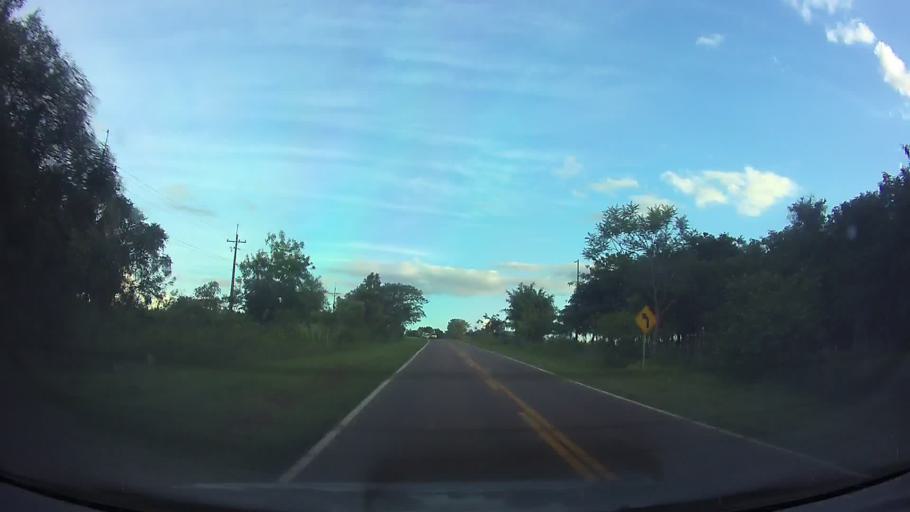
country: PY
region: Paraguari
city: Acahay
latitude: -25.8463
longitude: -57.1452
